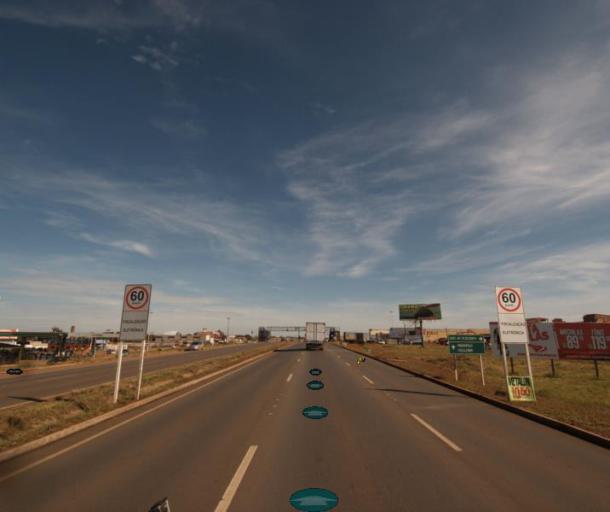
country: BR
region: Federal District
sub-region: Brasilia
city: Brasilia
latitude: -15.7526
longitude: -48.2592
